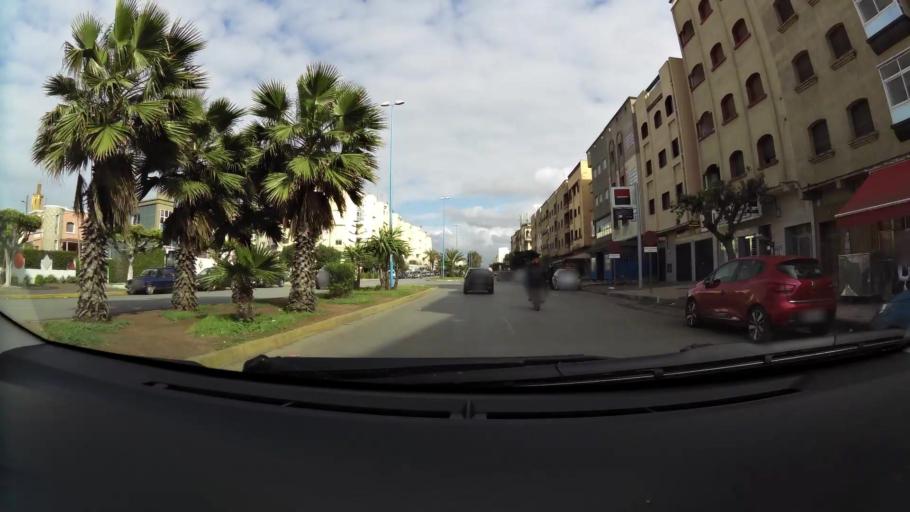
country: MA
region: Grand Casablanca
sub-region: Mohammedia
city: Mohammedia
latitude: 33.6940
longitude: -7.3785
